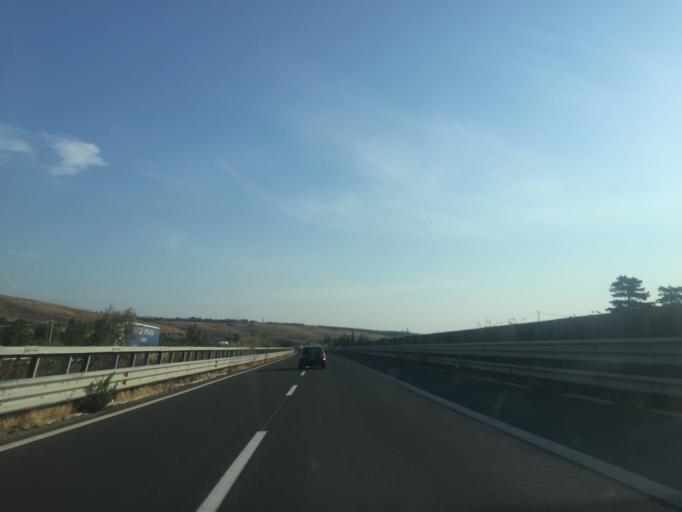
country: IT
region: Sicily
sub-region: Provincia di Siracusa
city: Carlentini
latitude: 37.3515
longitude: 15.0460
